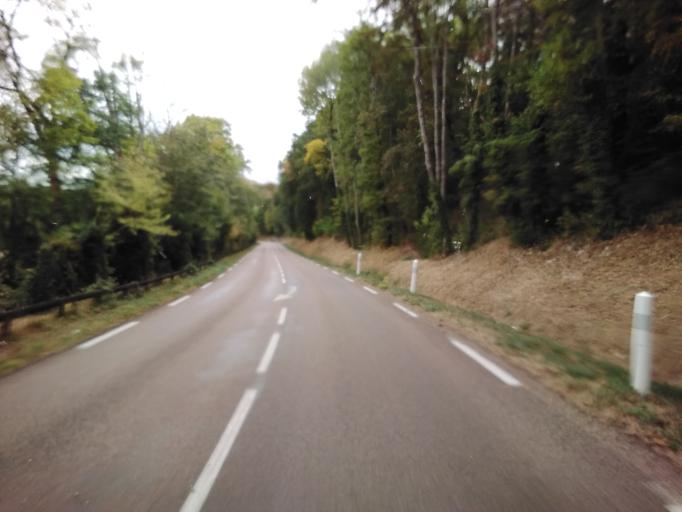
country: FR
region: Champagne-Ardenne
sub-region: Departement de l'Aube
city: Bar-sur-Seine
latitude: 48.1360
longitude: 4.3922
